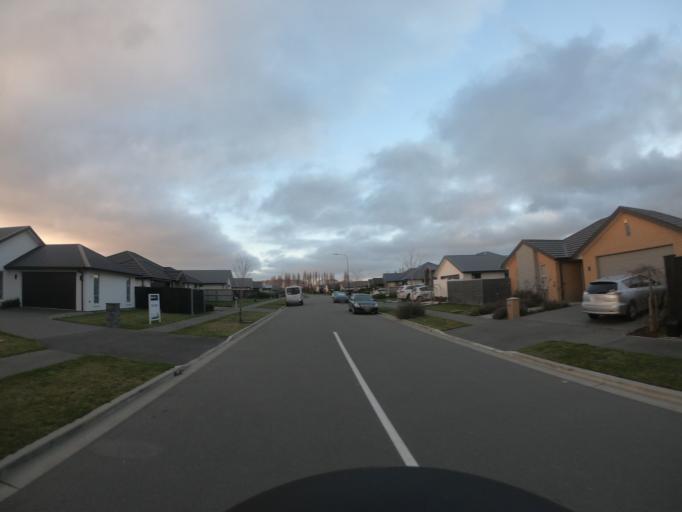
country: NZ
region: Canterbury
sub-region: Selwyn District
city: Prebbleton
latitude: -43.5638
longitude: 172.5581
